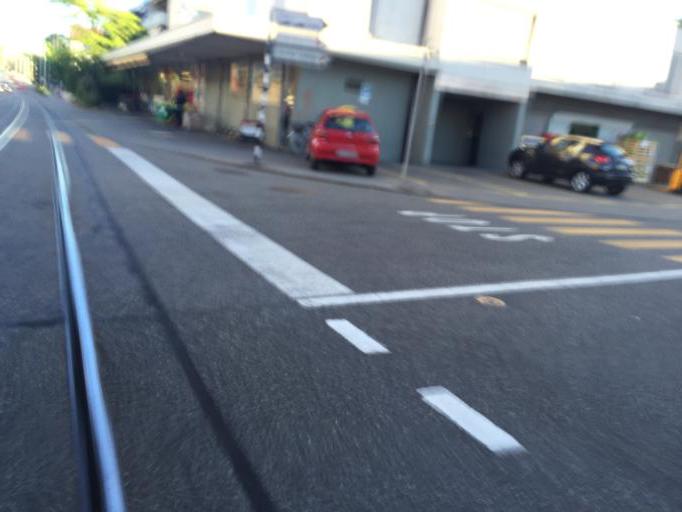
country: CH
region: Bern
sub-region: Bern-Mittelland District
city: Koniz
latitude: 46.9440
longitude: 7.3998
